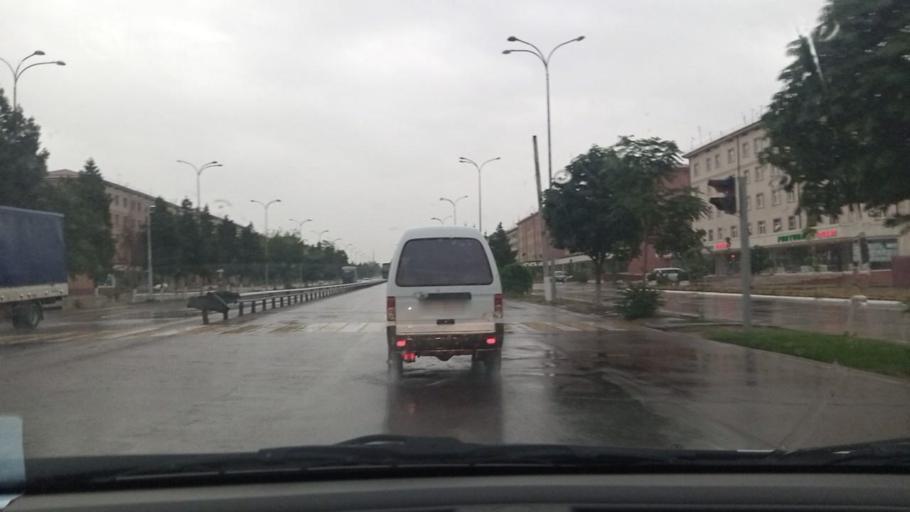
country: UZ
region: Toshkent
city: Ohangaron
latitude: 40.9088
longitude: 69.6255
